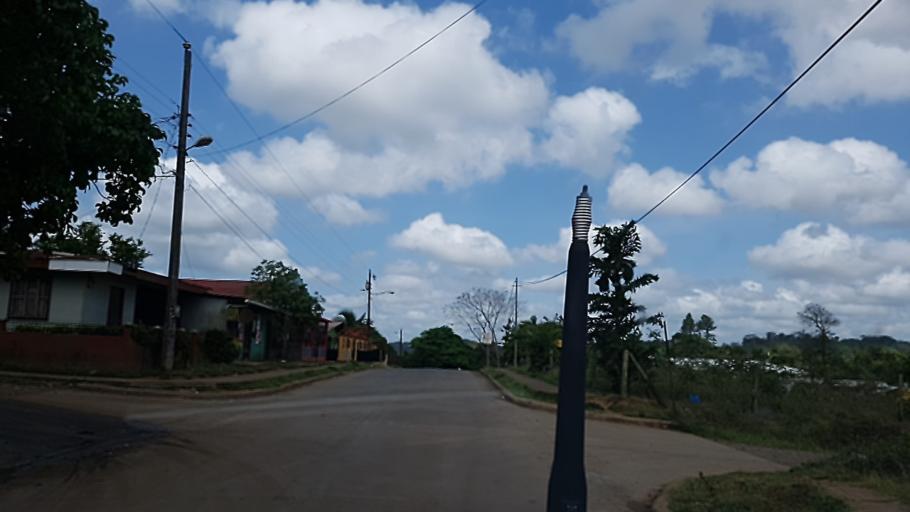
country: NI
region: Atlantico Sur
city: Nueva Guinea
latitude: 11.6862
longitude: -84.4586
